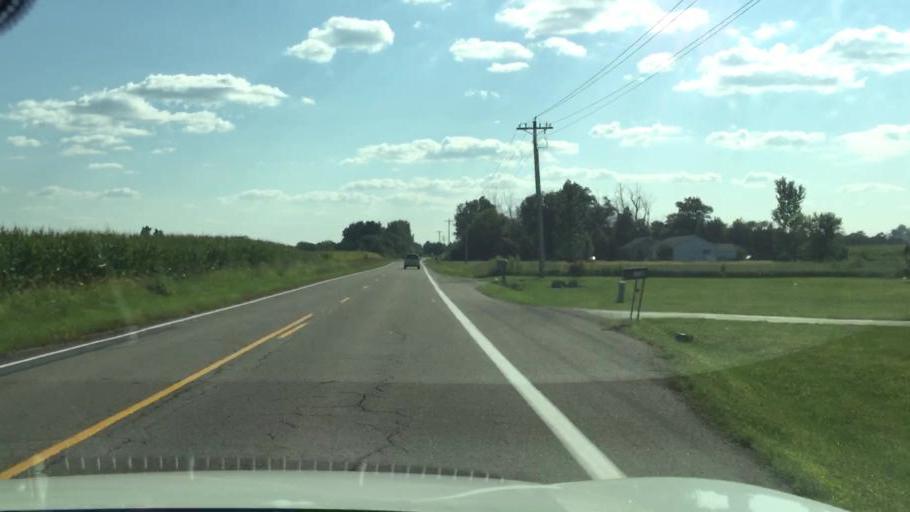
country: US
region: Ohio
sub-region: Champaign County
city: Mechanicsburg
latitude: 40.1090
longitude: -83.5269
